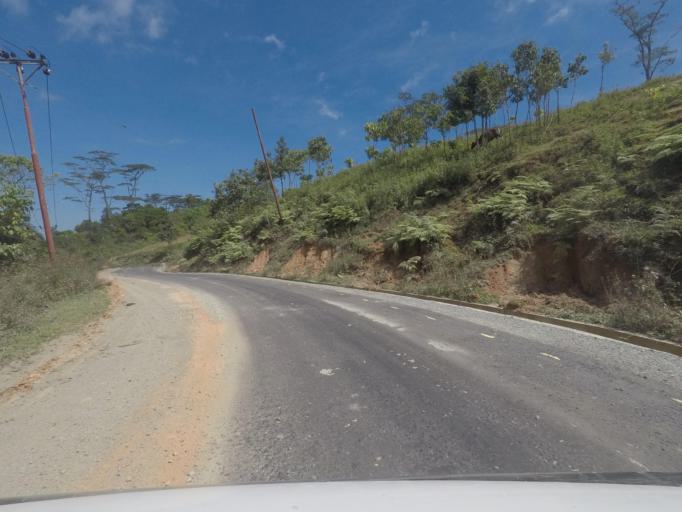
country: TL
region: Ermera
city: Gleno
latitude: -8.7485
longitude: 125.3413
